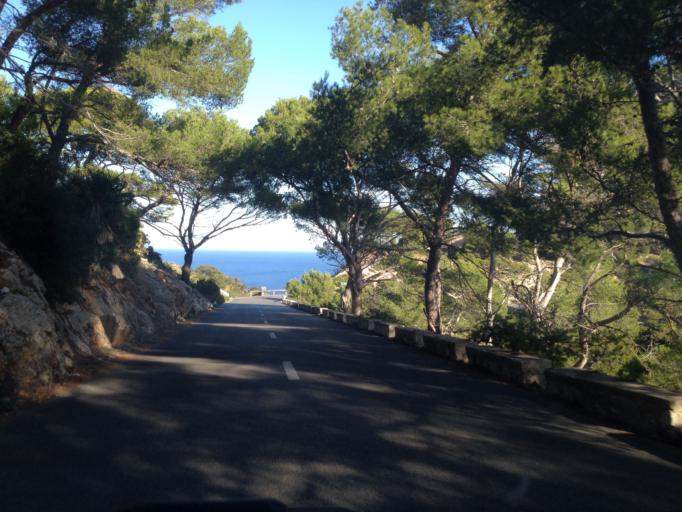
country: ES
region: Balearic Islands
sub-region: Illes Balears
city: Alcudia
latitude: 39.9324
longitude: 3.1252
